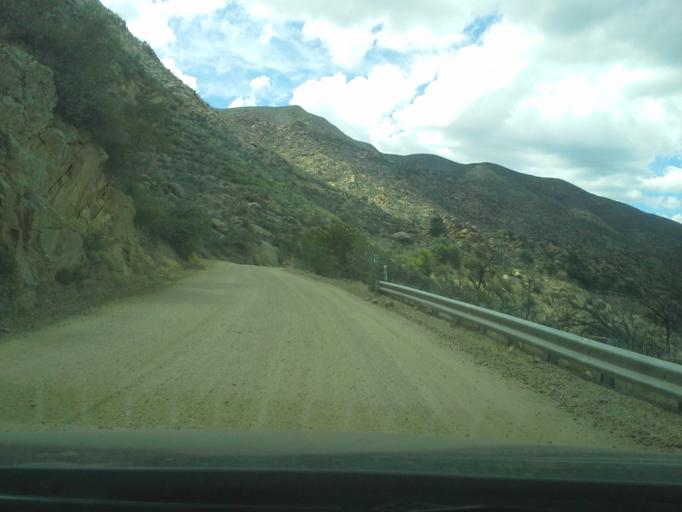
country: US
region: Arizona
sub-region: Yavapai County
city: Mayer
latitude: 34.2501
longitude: -112.2983
